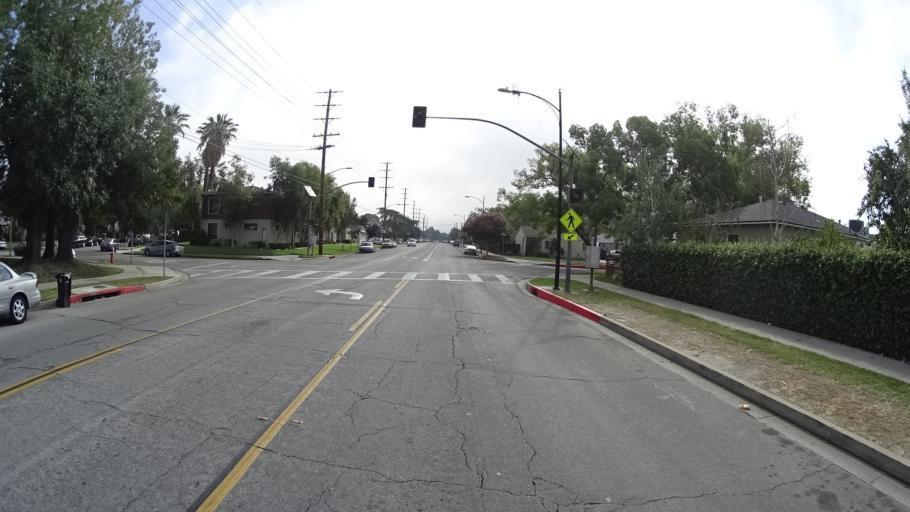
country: US
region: California
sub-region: Los Angeles County
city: Burbank
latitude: 34.1693
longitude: -118.3187
